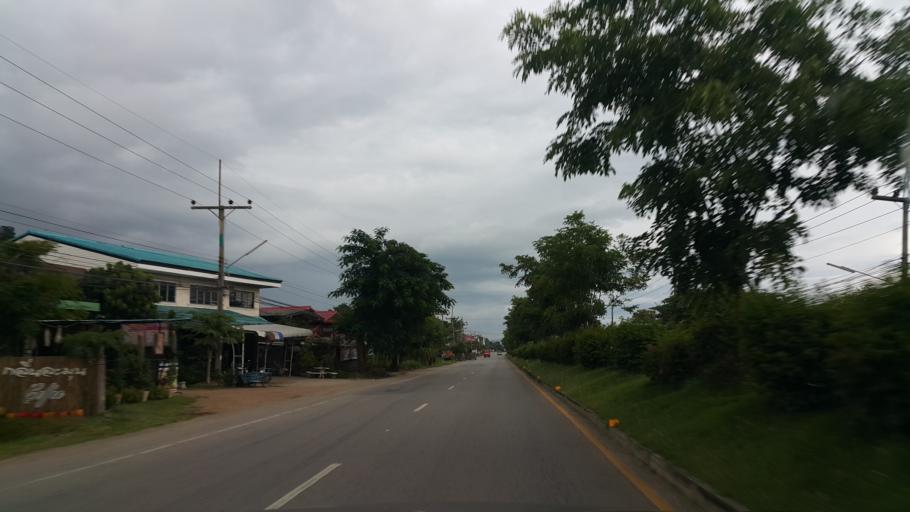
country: TH
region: Phayao
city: Dok Kham Tai
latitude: 19.1489
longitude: 99.9318
